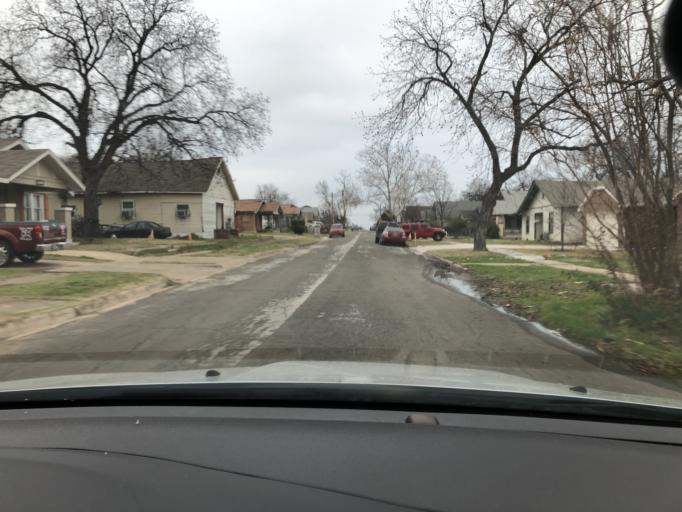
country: US
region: Texas
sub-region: Tarrant County
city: Fort Worth
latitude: 32.7252
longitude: -97.3152
